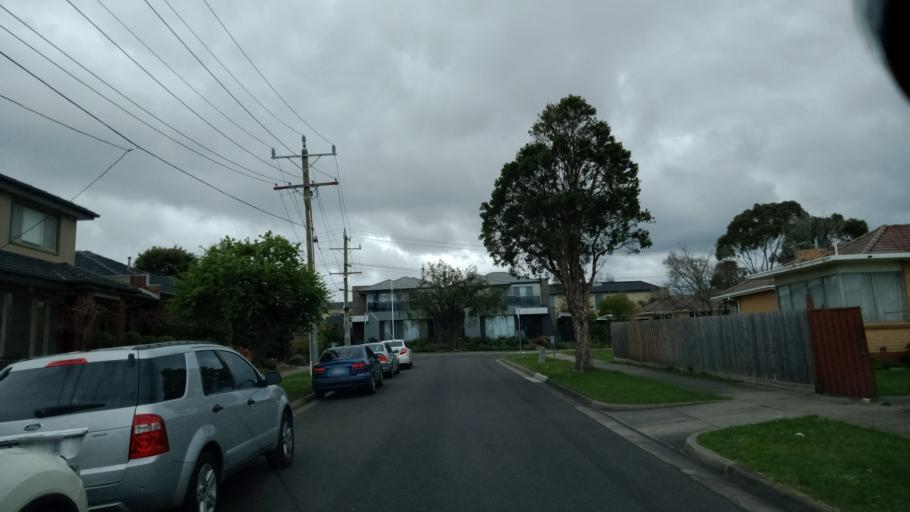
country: AU
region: Victoria
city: Burwood East
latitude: -37.8780
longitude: 145.1601
